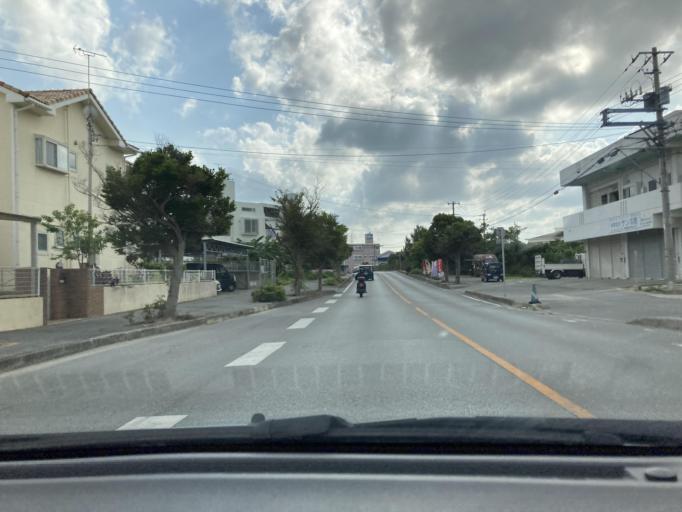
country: JP
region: Okinawa
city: Tomigusuku
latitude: 26.1676
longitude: 127.7371
